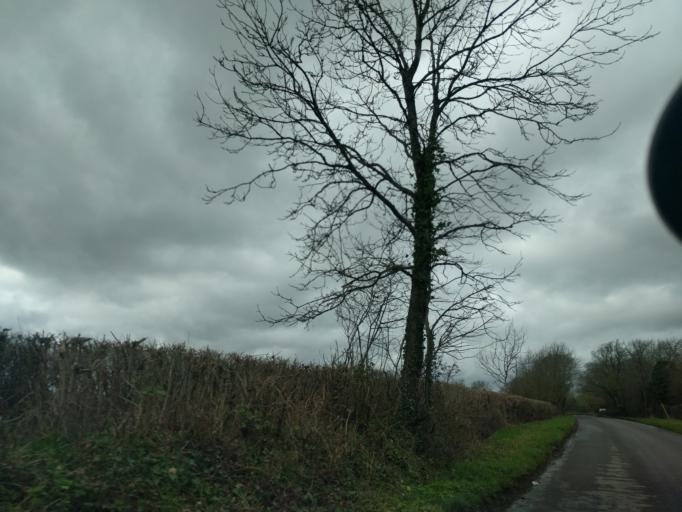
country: GB
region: England
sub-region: Wiltshire
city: Norton
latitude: 51.5614
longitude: -2.1911
